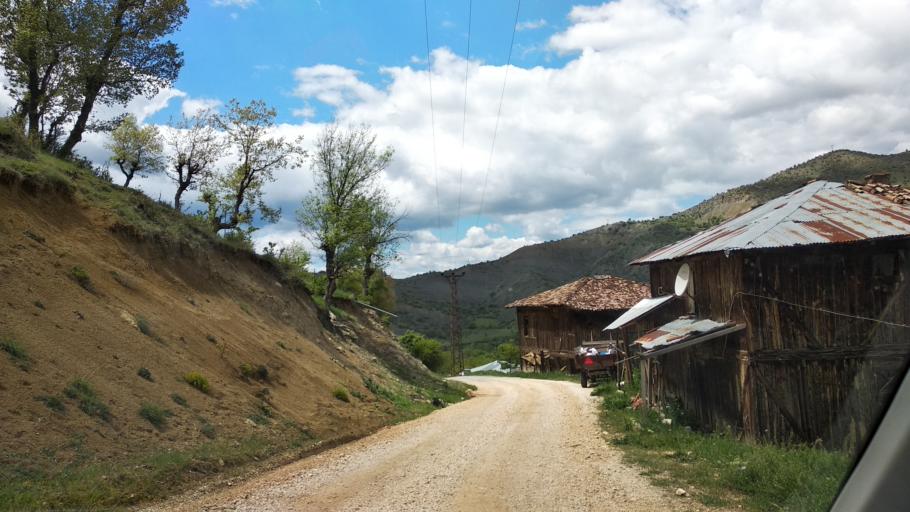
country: TR
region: Bolu
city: Seben
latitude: 40.4279
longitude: 31.5966
